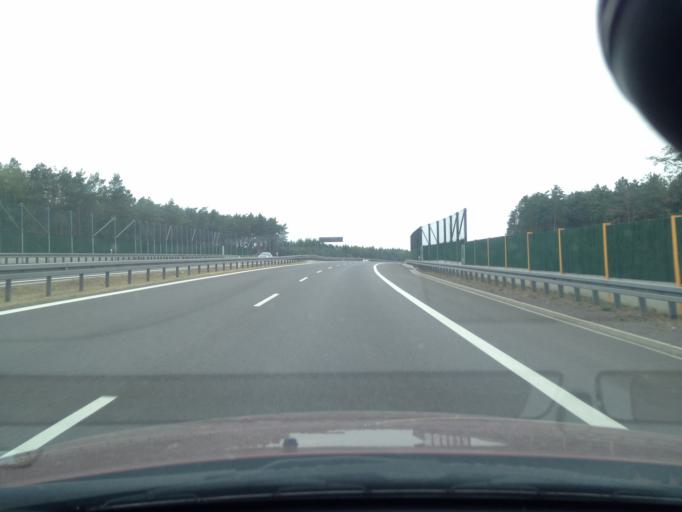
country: PL
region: Lubusz
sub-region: Powiat miedzyrzecki
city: Skwierzyna
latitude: 52.5600
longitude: 15.4762
